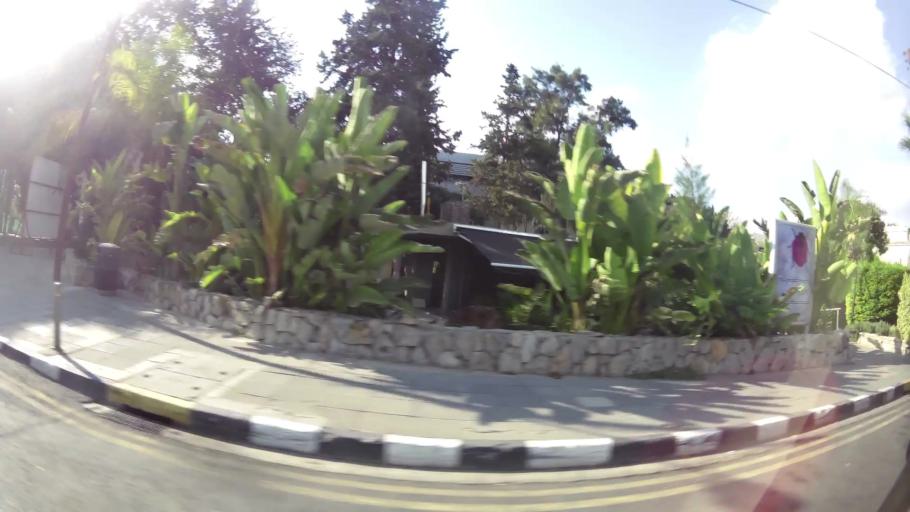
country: CY
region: Lefkosia
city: Nicosia
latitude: 35.1718
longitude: 33.3551
